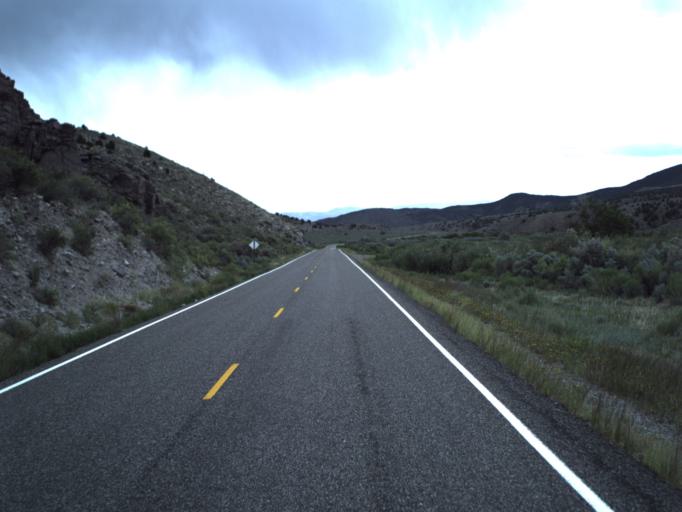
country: US
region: Utah
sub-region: Piute County
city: Junction
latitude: 38.1869
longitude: -112.0889
